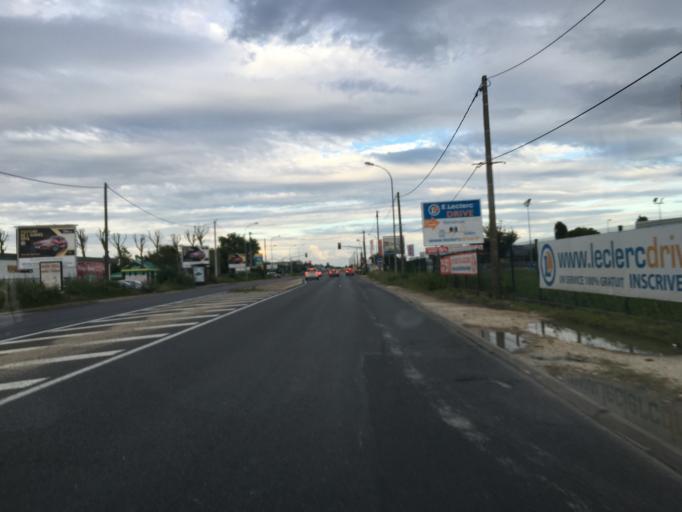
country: FR
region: Ile-de-France
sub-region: Departement de Seine-et-Marne
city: Servon
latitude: 48.7124
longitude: 2.5795
